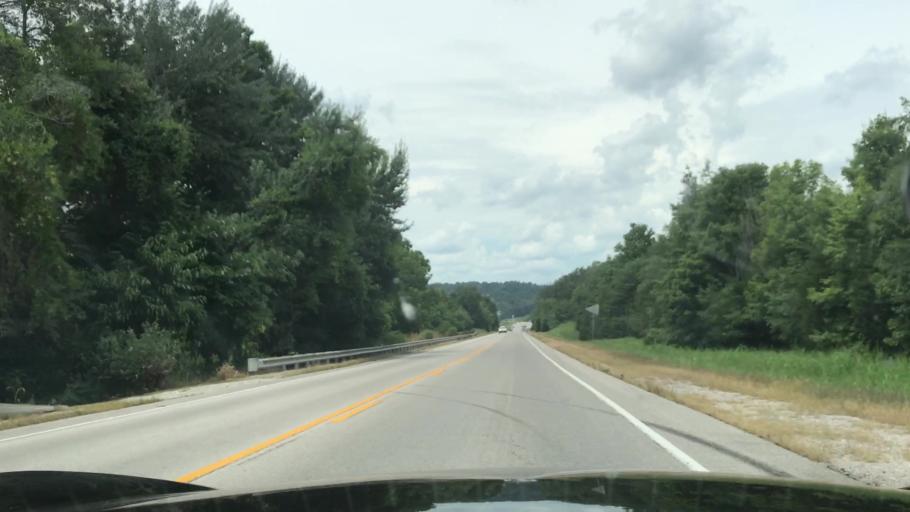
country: US
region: Kentucky
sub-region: Hart County
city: Horse Cave
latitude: 37.1953
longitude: -85.9271
